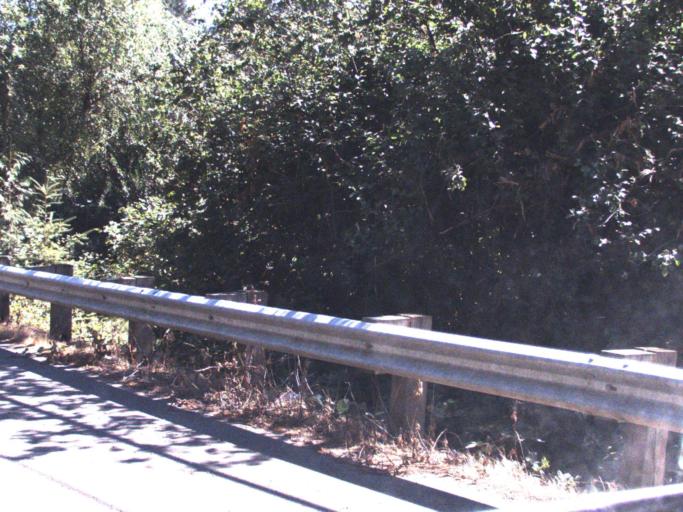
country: US
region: Washington
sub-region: King County
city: Issaquah
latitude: 47.5292
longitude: -122.0621
